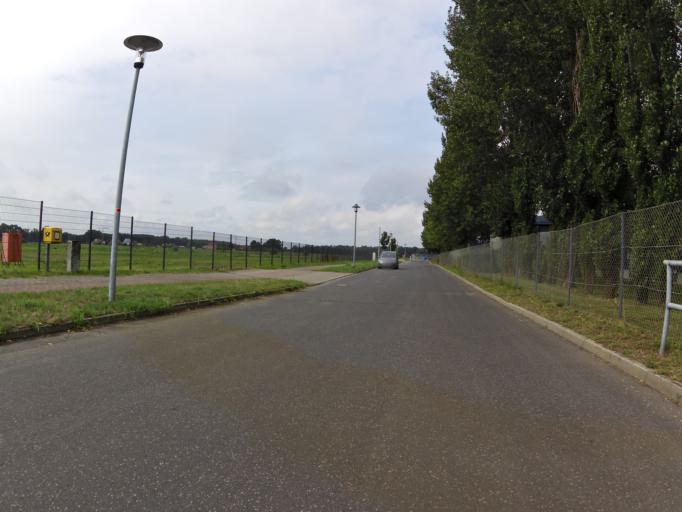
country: DE
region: Brandenburg
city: Storkow
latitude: 52.2683
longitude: 13.9372
